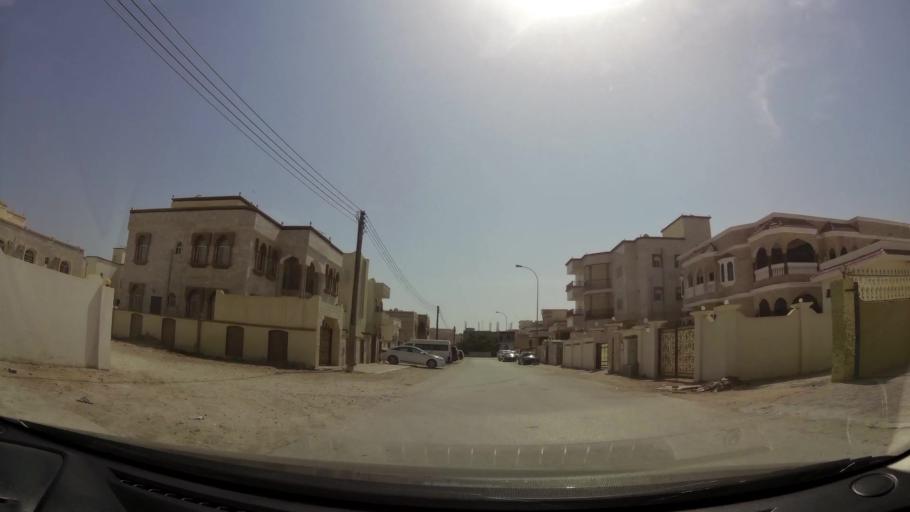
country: OM
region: Zufar
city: Salalah
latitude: 17.0487
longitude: 54.1565
